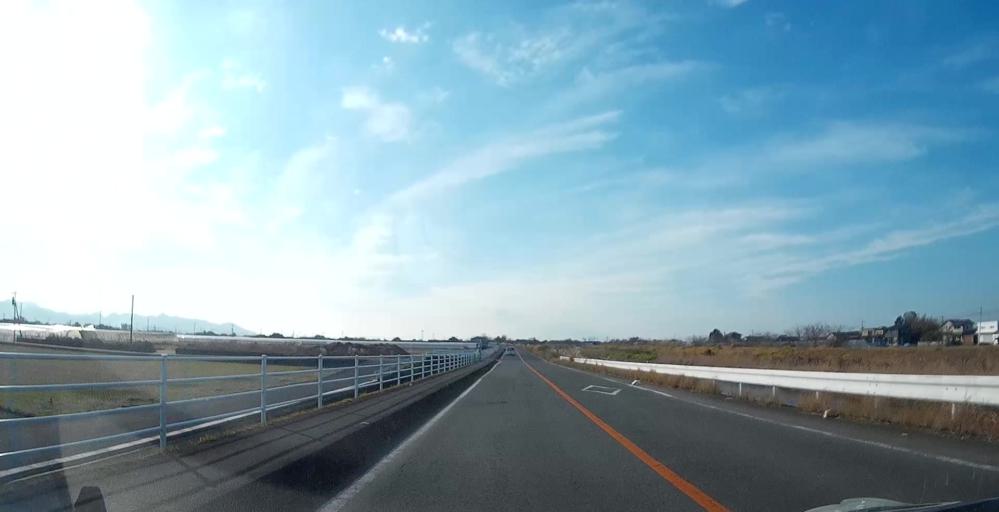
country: JP
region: Kumamoto
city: Uto
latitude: 32.7328
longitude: 130.6584
